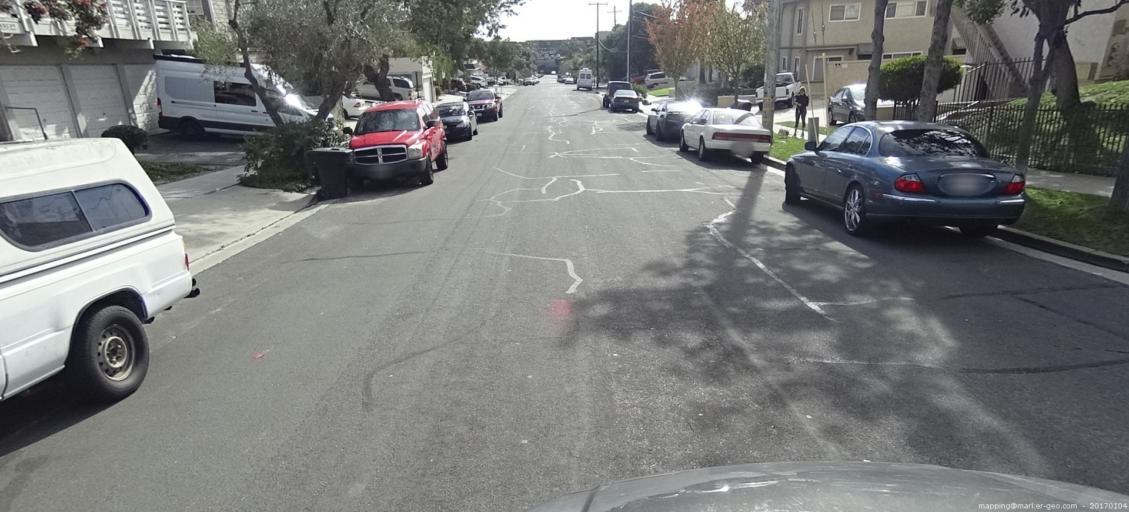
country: US
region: California
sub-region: Orange County
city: Dana Point
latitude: 33.4703
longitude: -117.6964
